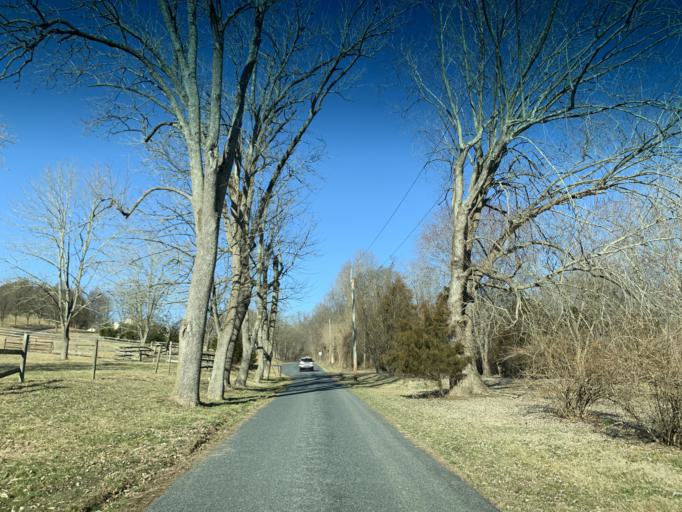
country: US
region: Maryland
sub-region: Harford County
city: South Bel Air
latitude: 39.6180
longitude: -76.2409
